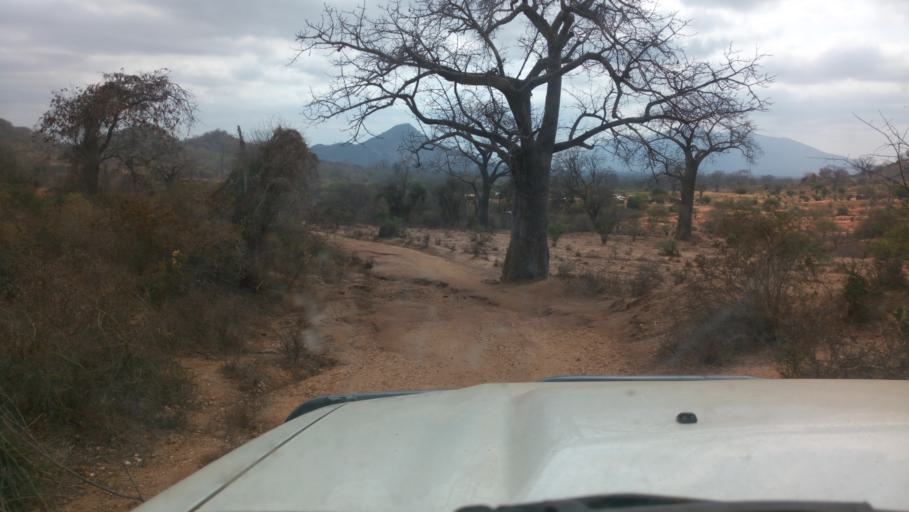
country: KE
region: Kitui
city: Kitui
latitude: -1.8414
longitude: 38.2990
